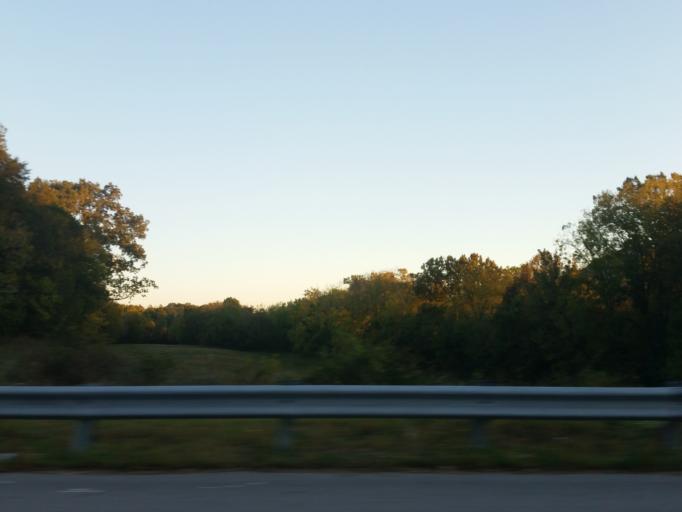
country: US
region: Tennessee
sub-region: Grainger County
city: Blaine
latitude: 36.1519
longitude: -83.7525
